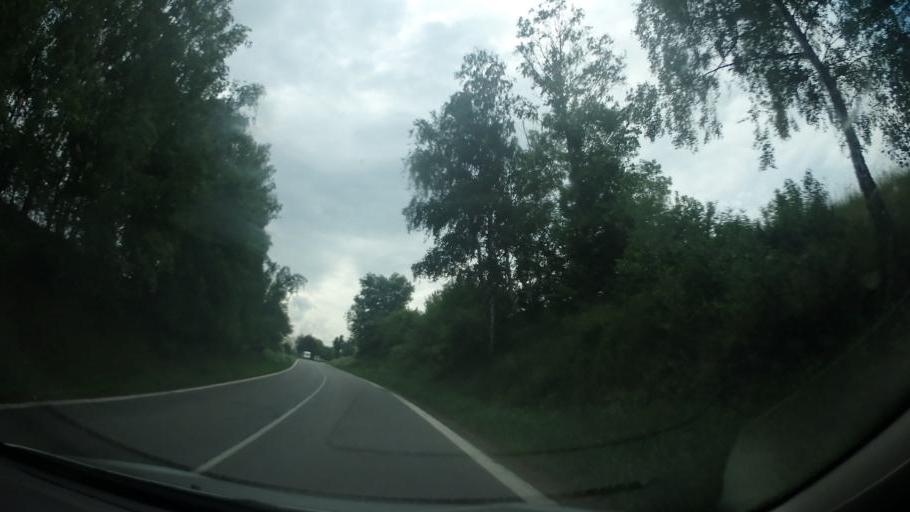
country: CZ
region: Vysocina
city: Bystrice nad Pernstejnem
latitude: 49.5209
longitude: 16.3015
